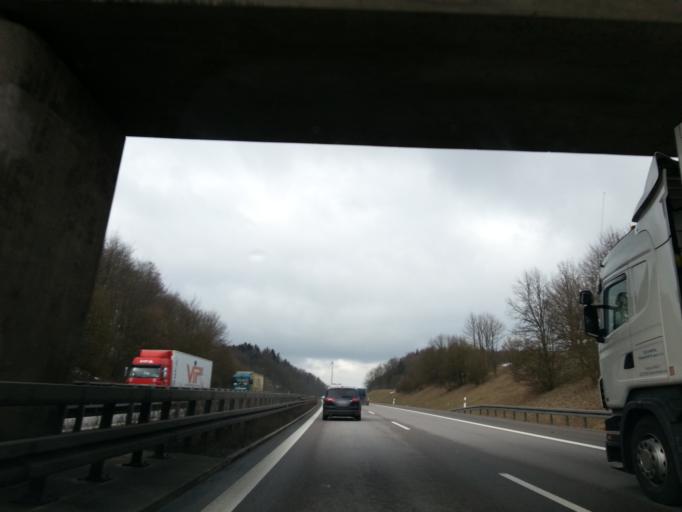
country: DE
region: Bavaria
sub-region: Upper Palatinate
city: Brunn
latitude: 49.1325
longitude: 11.8674
